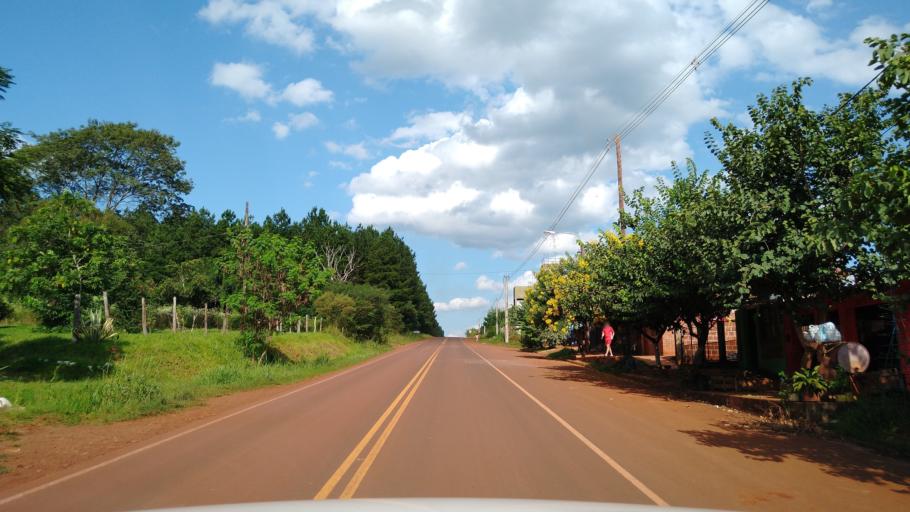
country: AR
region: Misiones
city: Puerto Piray
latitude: -26.4724
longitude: -54.6894
